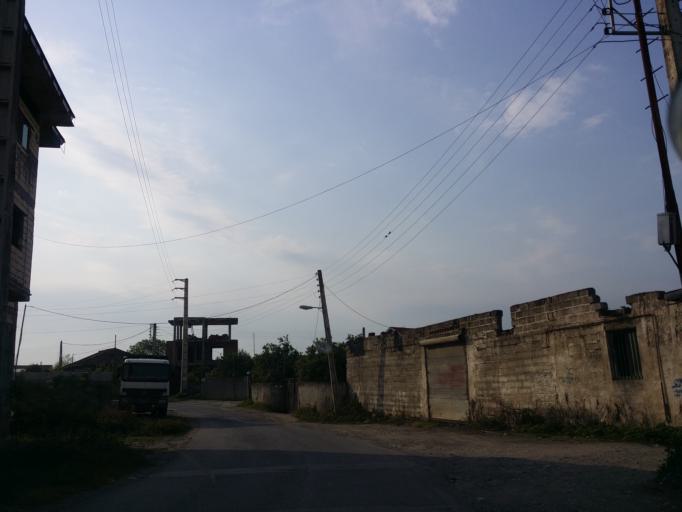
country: IR
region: Mazandaran
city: Chalus
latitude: 36.6652
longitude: 51.3747
